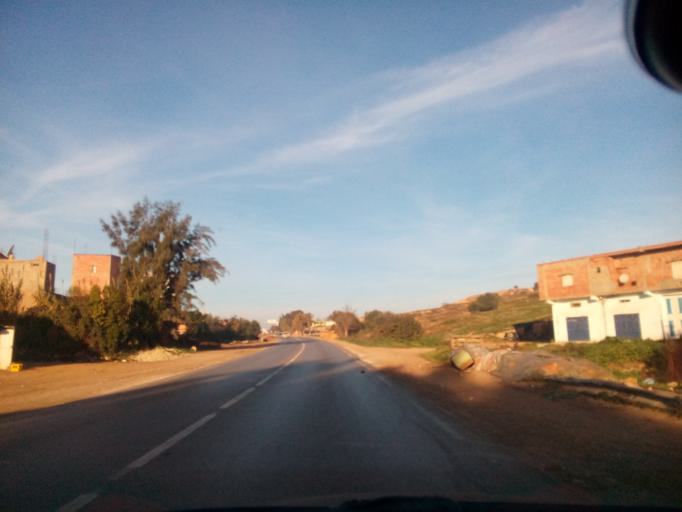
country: DZ
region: Relizane
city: Relizane
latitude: 35.7188
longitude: 0.3289
